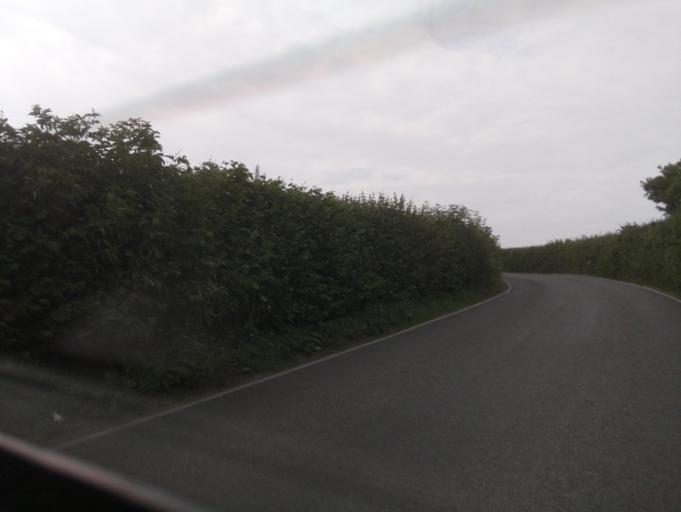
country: GB
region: England
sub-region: Devon
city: Colyton
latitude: 50.7074
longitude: -3.1015
